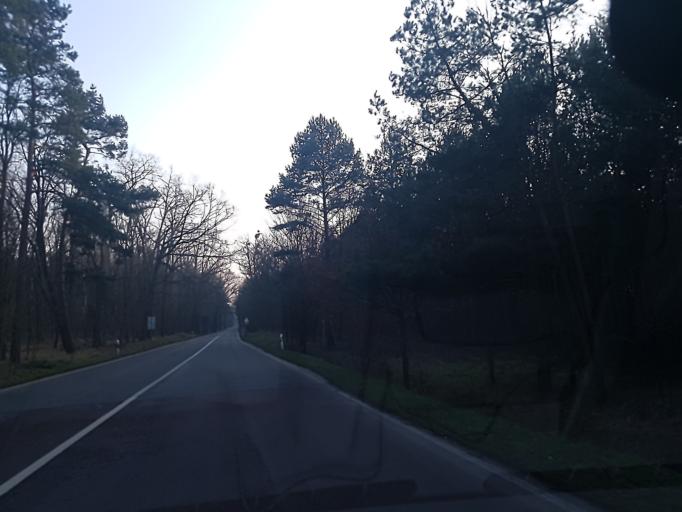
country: DE
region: Saxony-Anhalt
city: Coswig
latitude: 51.9545
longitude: 12.4633
